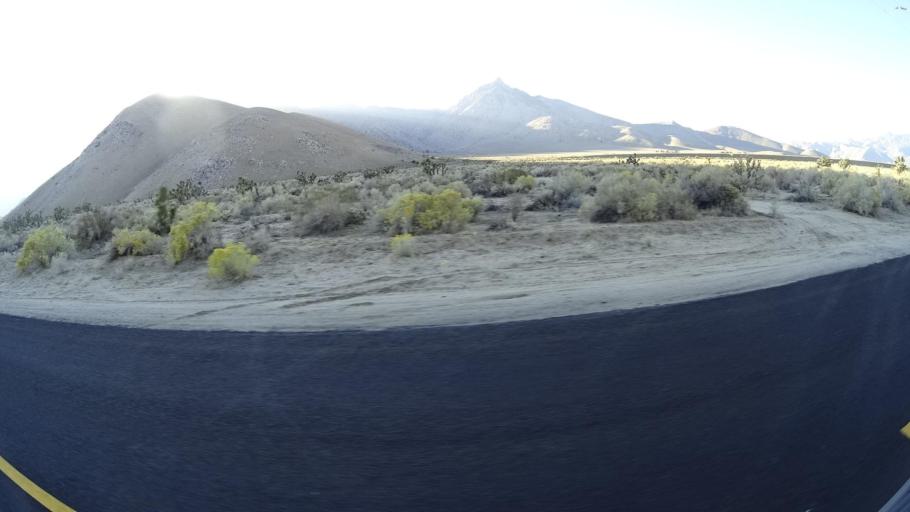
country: US
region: California
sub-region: Kern County
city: Weldon
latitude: 35.6161
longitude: -118.2434
